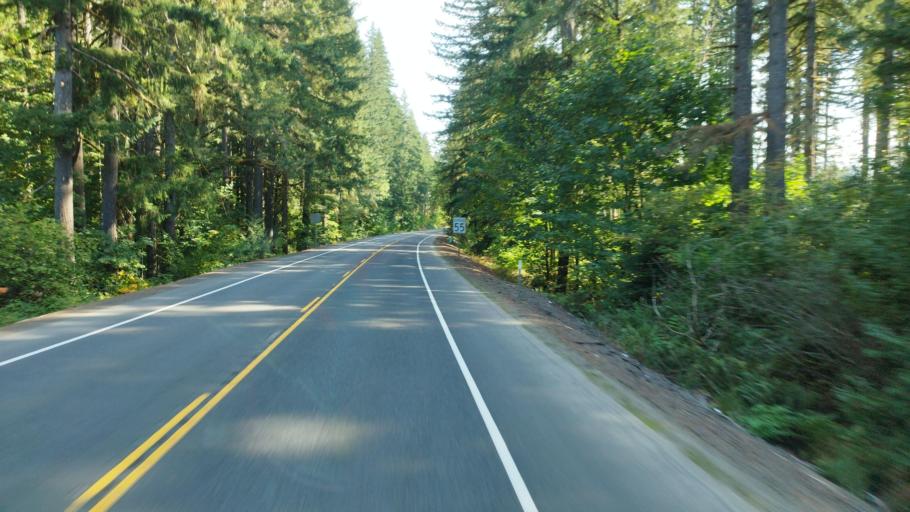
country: US
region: Oregon
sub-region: Columbia County
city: Vernonia
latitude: 45.7751
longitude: -123.3278
